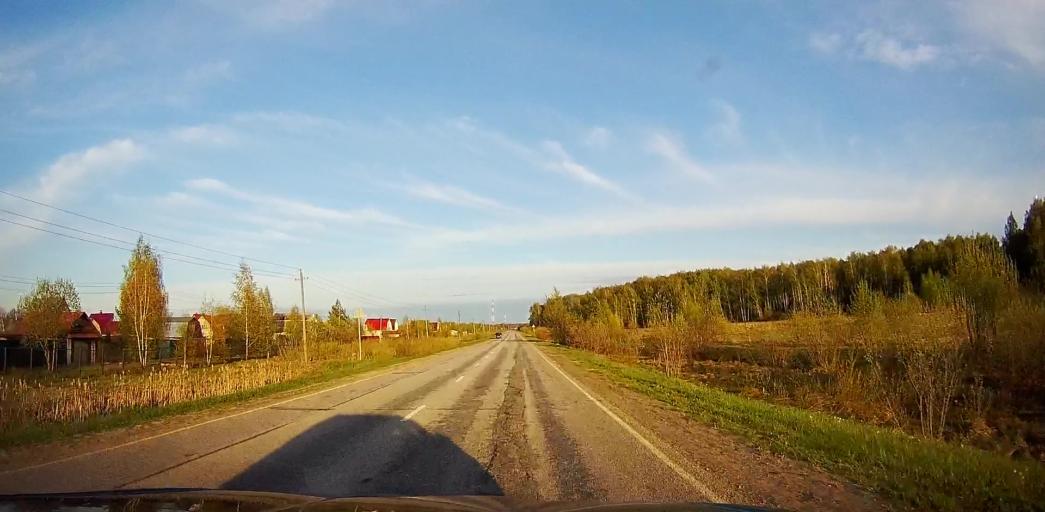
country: RU
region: Moskovskaya
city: Meshcherino
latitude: 55.2393
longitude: 38.3418
